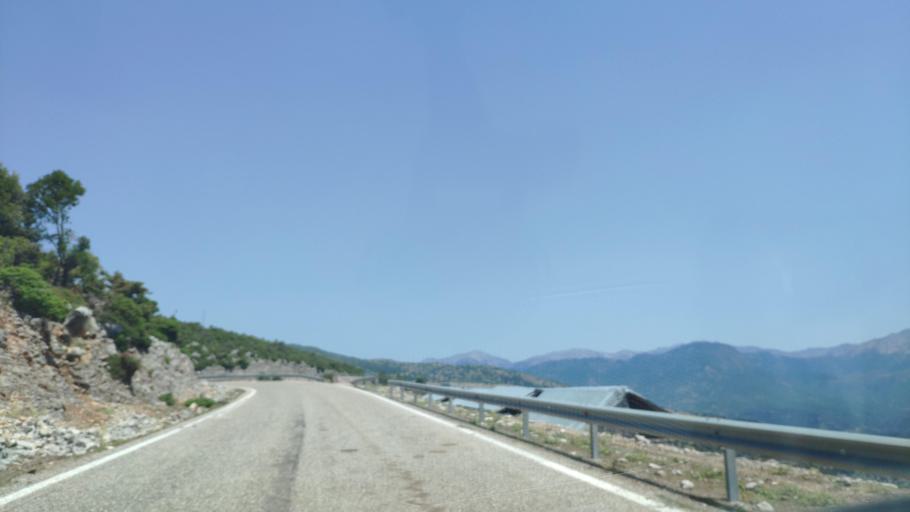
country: GR
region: West Greece
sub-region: Nomos Aitolias kai Akarnanias
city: Krikellos
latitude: 39.0536
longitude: 21.3838
